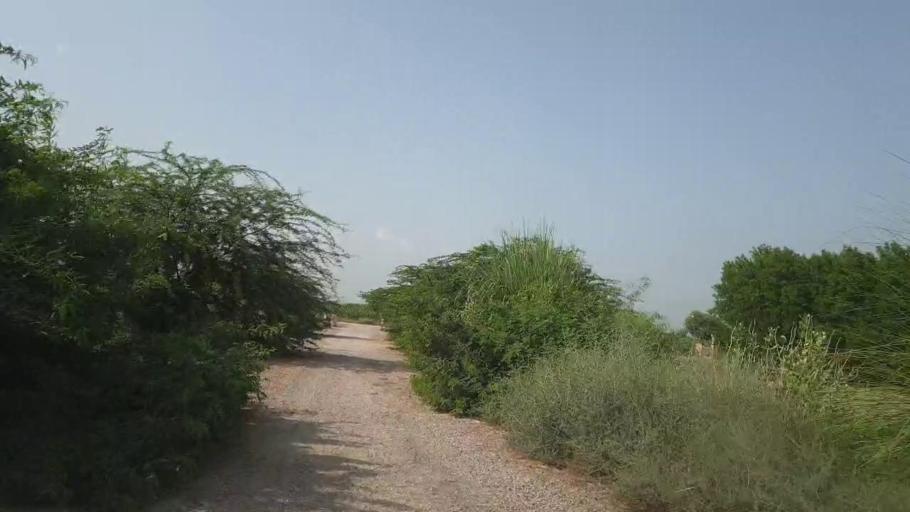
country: PK
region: Sindh
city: Pano Aqil
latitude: 27.7820
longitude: 69.1599
